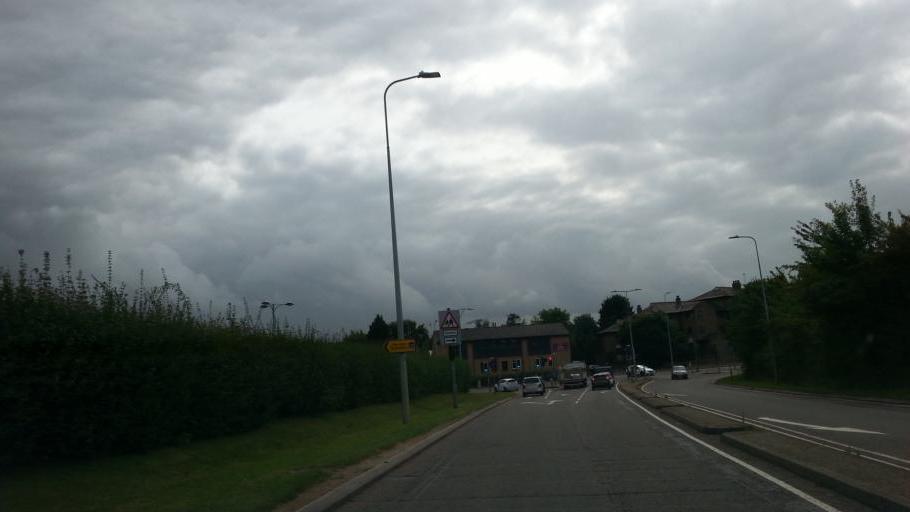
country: GB
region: England
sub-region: Essex
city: Chelmsford
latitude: 51.7416
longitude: 0.4692
